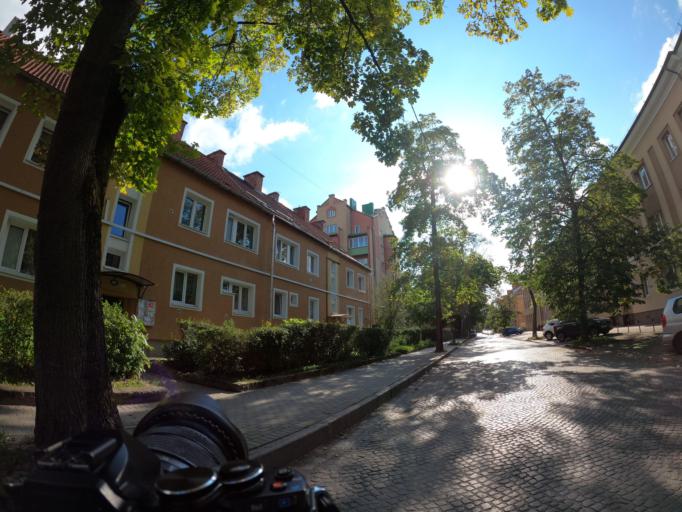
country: RU
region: Kaliningrad
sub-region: Gorod Kaliningrad
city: Kaliningrad
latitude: 54.7262
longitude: 20.4679
